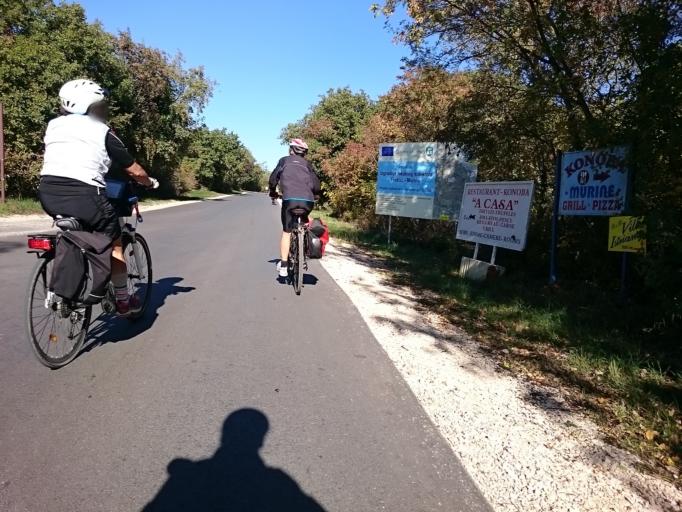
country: HR
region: Istarska
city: Umag
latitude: 45.4552
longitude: 13.5379
